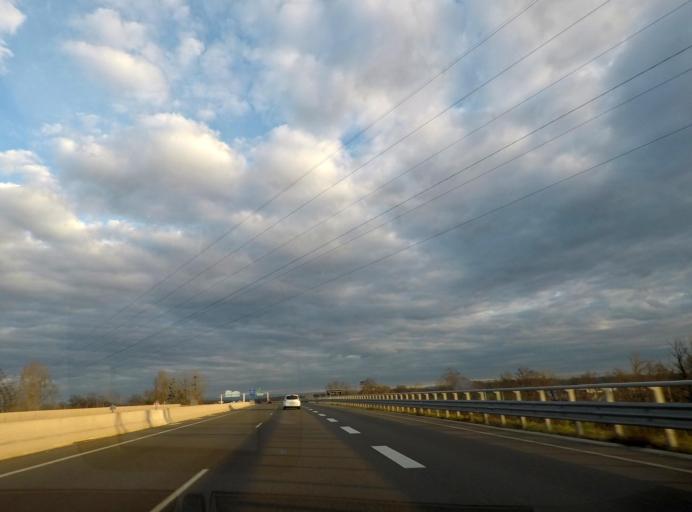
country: FR
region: Bourgogne
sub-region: Departement de Saone-et-Loire
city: Charnay-les-Macon
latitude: 46.2782
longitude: 4.7986
